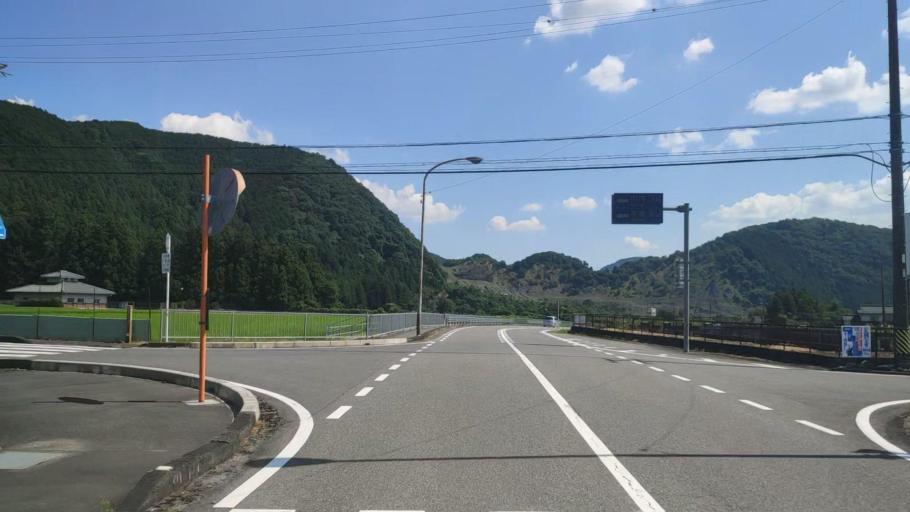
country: JP
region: Gifu
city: Godo
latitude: 35.5340
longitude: 136.6512
